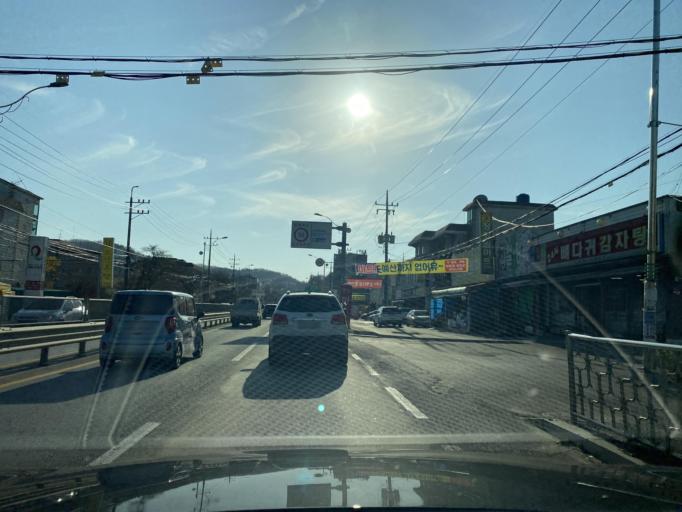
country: KR
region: Chungcheongnam-do
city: Asan
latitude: 36.7764
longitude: 126.9339
